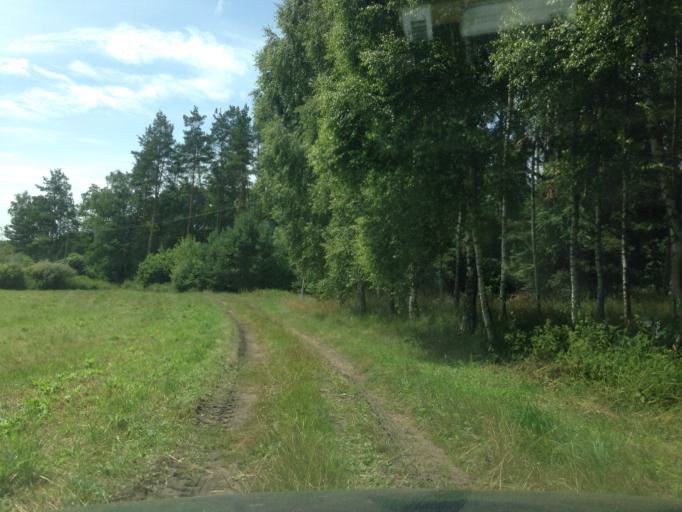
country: PL
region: Kujawsko-Pomorskie
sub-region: Powiat brodnicki
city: Bartniczka
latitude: 53.2684
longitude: 19.5863
